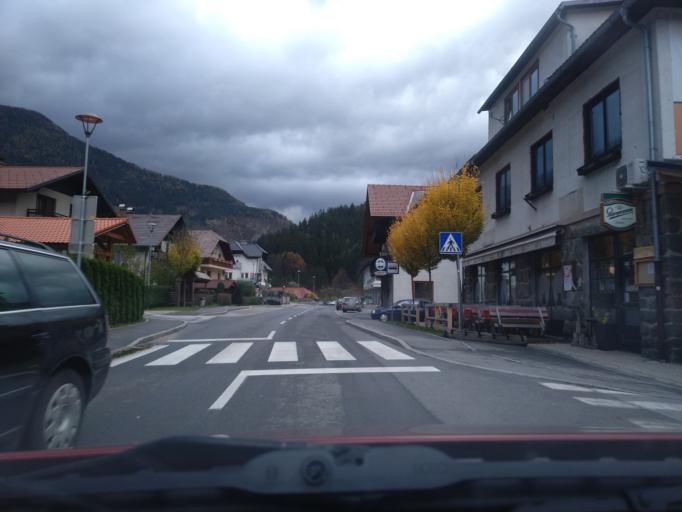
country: SI
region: Luce
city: Luce
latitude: 46.3554
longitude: 14.7445
